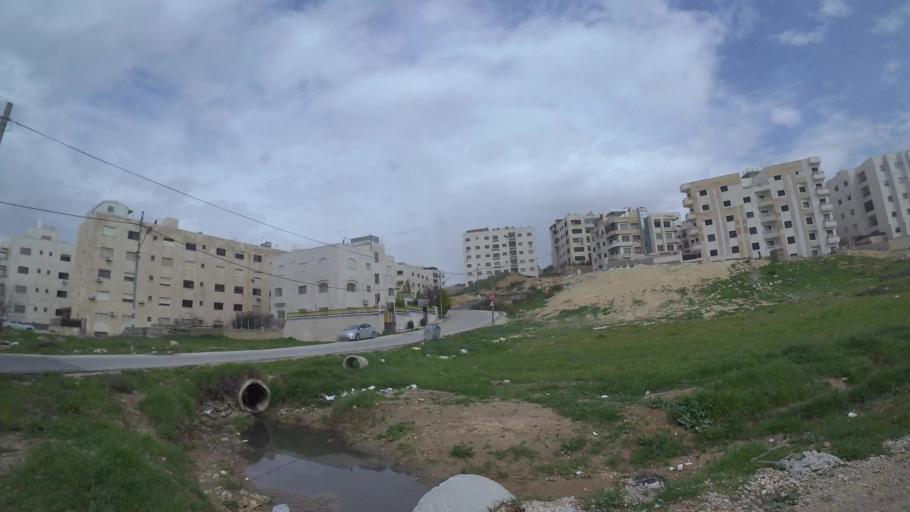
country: JO
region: Amman
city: Umm as Summaq
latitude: 31.9070
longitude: 35.8499
